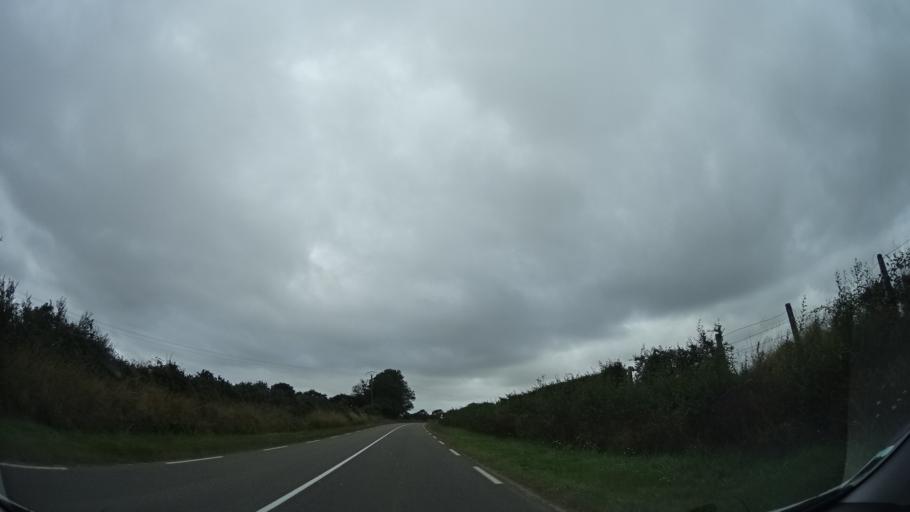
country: FR
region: Lower Normandy
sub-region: Departement de la Manche
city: Portbail
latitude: 49.3186
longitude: -1.6231
